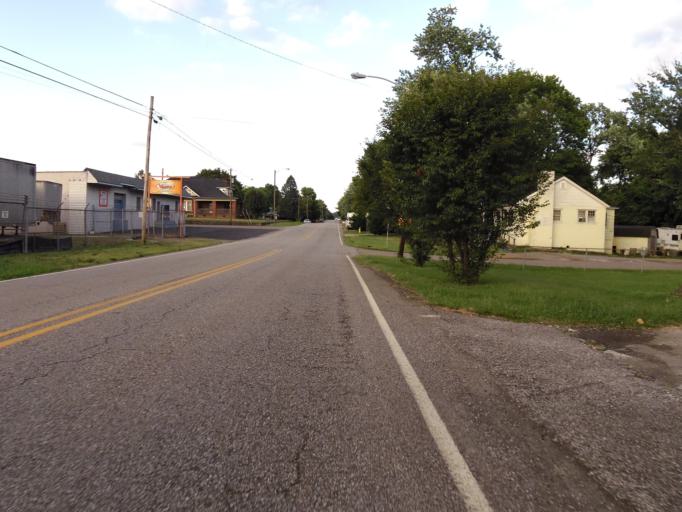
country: US
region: Tennessee
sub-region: Knox County
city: Knoxville
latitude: 35.9979
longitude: -83.9355
